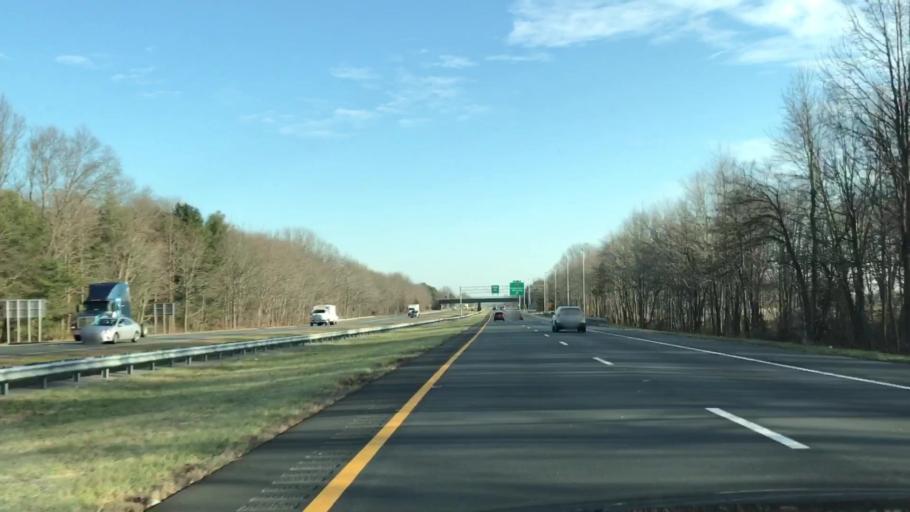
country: US
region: New Jersey
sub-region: Monmouth County
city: Allentown
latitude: 40.1877
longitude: -74.5765
